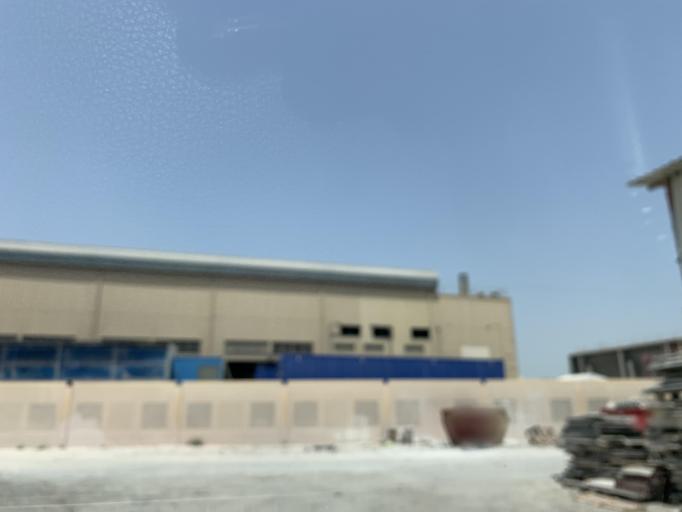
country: BH
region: Northern
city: Madinat `Isa
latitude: 26.1925
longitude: 50.5507
